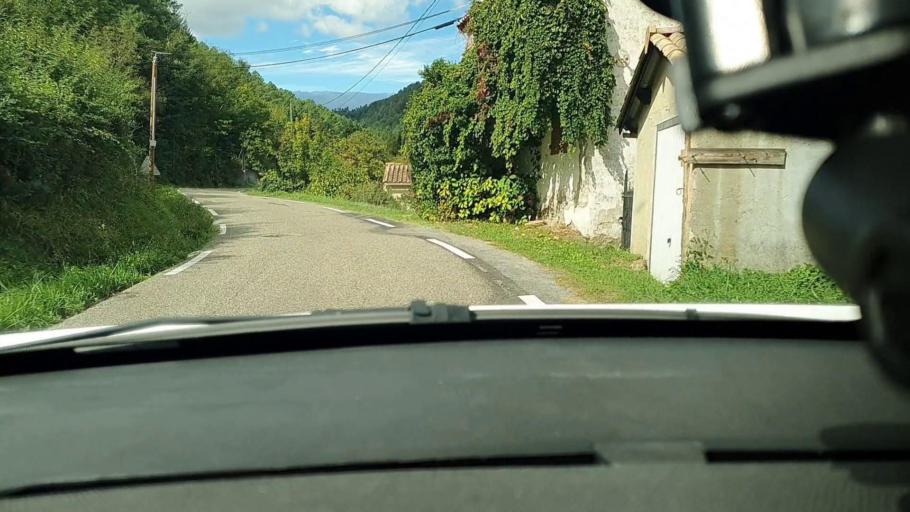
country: FR
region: Languedoc-Roussillon
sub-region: Departement du Gard
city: Besseges
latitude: 44.3016
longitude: 4.0173
